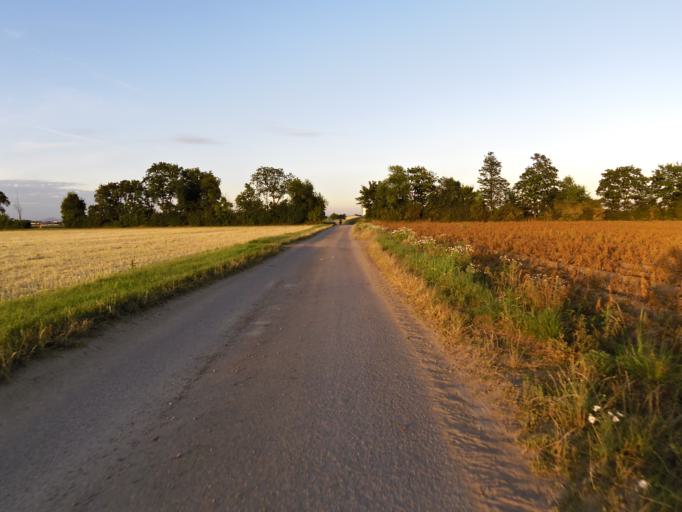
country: DE
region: Rheinland-Pfalz
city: Kleinniedesheim
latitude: 49.5746
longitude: 8.3373
